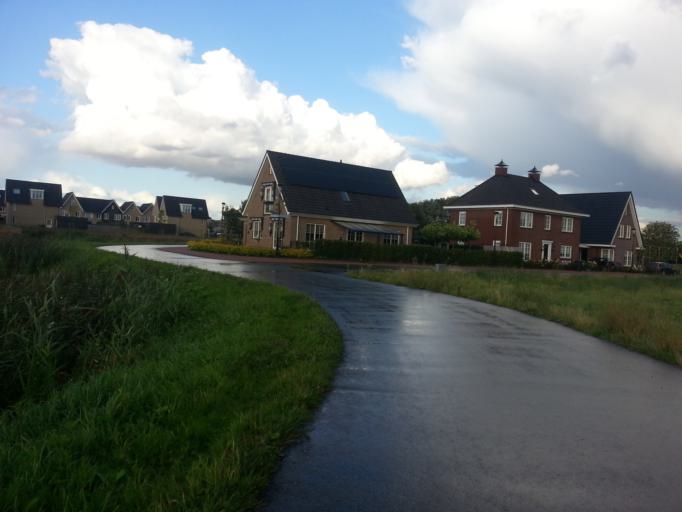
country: NL
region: South Holland
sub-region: Gemeente Spijkenisse
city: Spijkenisse
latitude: 51.8256
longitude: 4.2488
